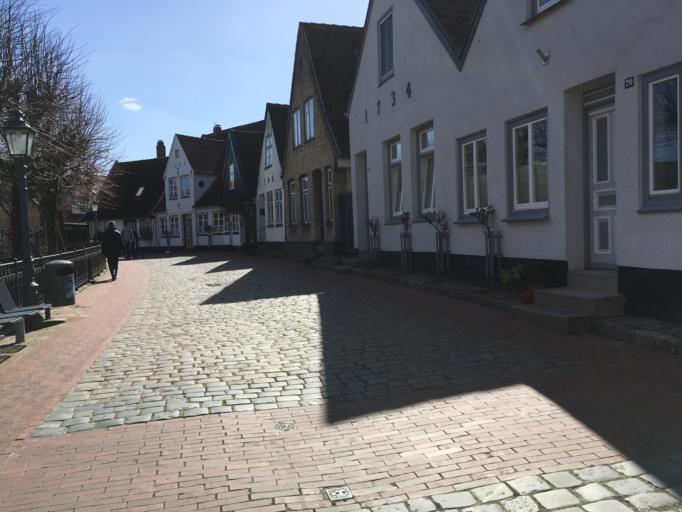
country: DE
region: Schleswig-Holstein
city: Schleswig
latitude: 54.5126
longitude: 9.5741
